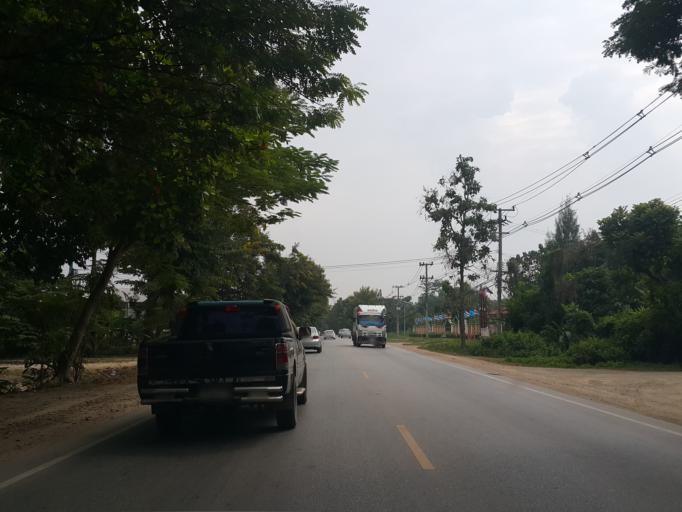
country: TH
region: Chiang Mai
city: San Sai
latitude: 18.9475
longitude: 98.9841
